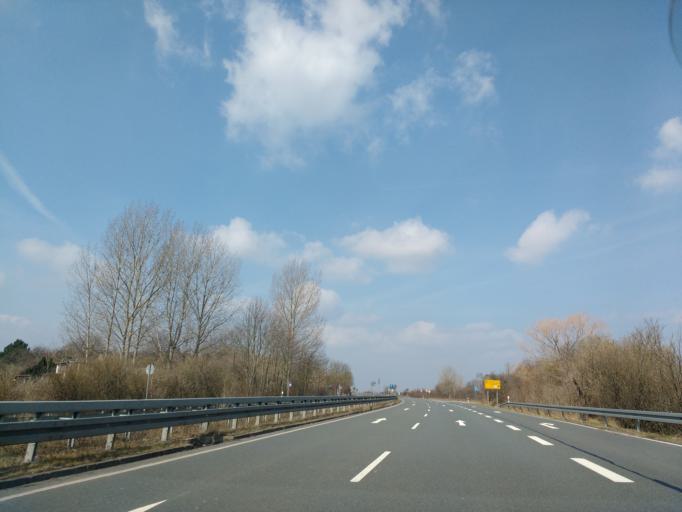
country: DE
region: Saxony-Anhalt
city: Roblingen am See
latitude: 51.4834
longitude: 11.7042
